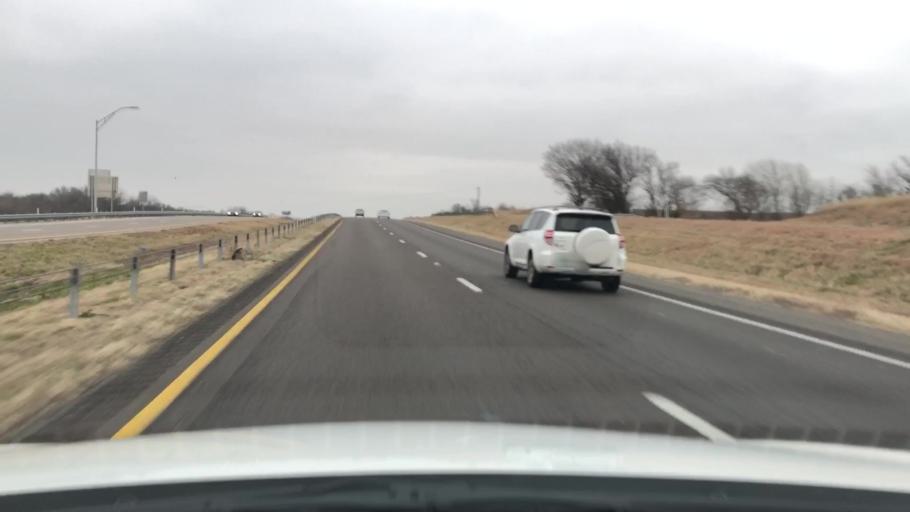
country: US
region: Texas
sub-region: Cooke County
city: Gainesville
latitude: 33.6961
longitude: -97.1625
